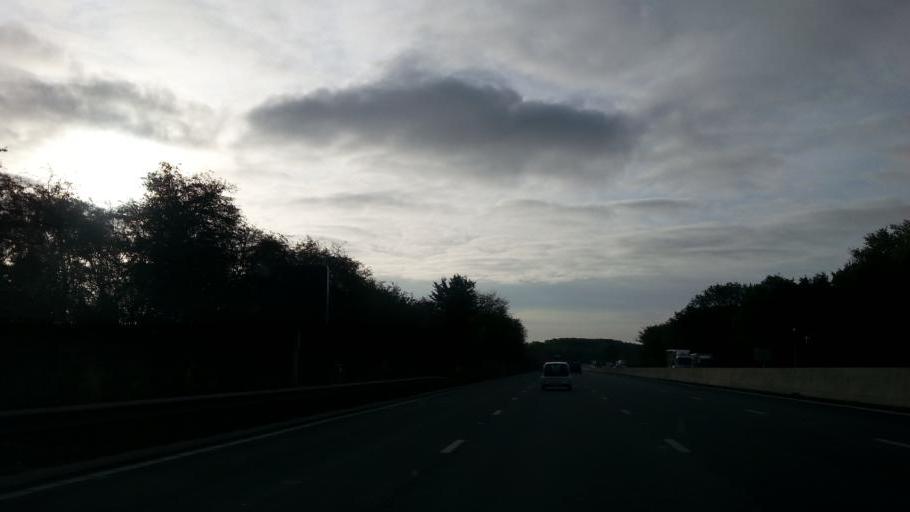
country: GB
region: England
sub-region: Northamptonshire
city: Long Buckby
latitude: 52.2829
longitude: -1.0997
